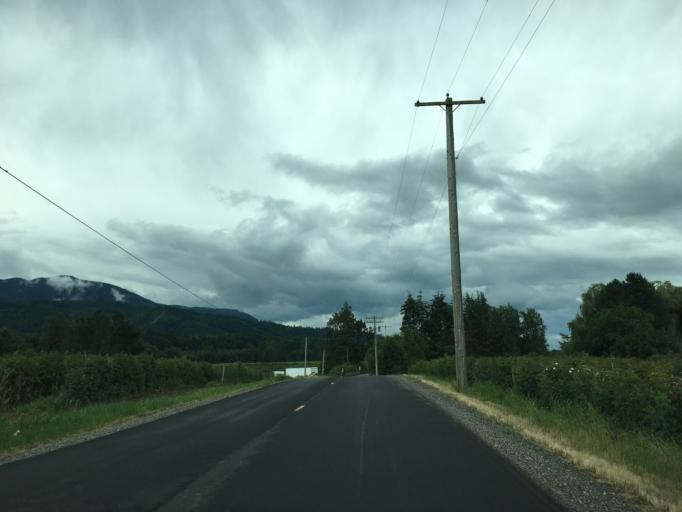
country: US
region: Washington
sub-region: Whatcom County
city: Sumas
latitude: 48.9792
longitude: -122.2538
